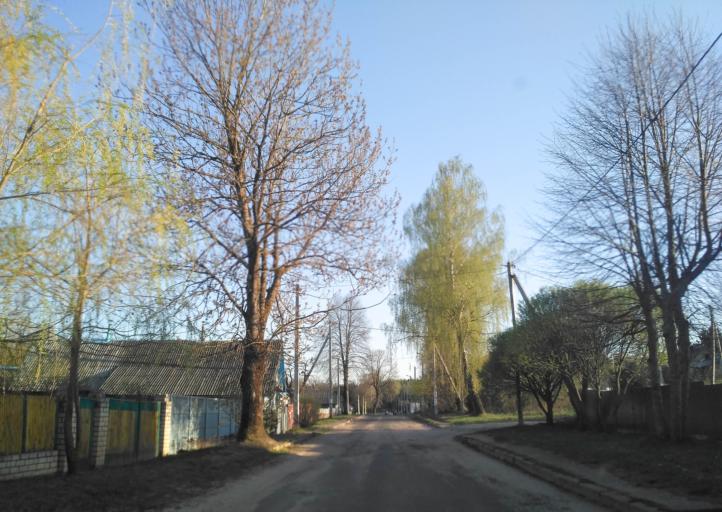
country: BY
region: Minsk
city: Pyatryshki
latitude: 54.0970
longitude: 27.1953
